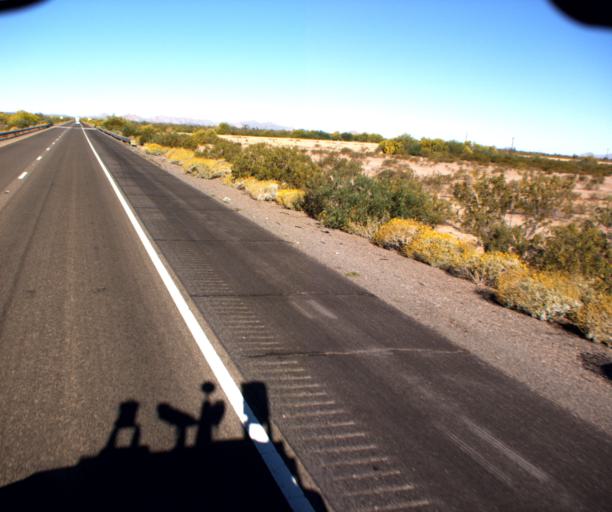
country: US
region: Arizona
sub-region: Pinal County
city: Casa Grande
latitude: 32.8288
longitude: -111.9778
